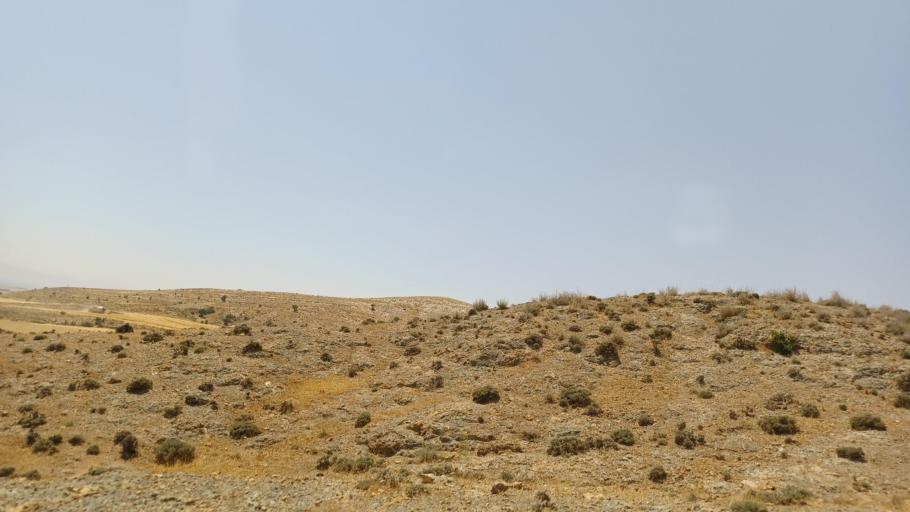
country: CY
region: Larnaka
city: Troulloi
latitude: 35.0002
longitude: 33.6163
